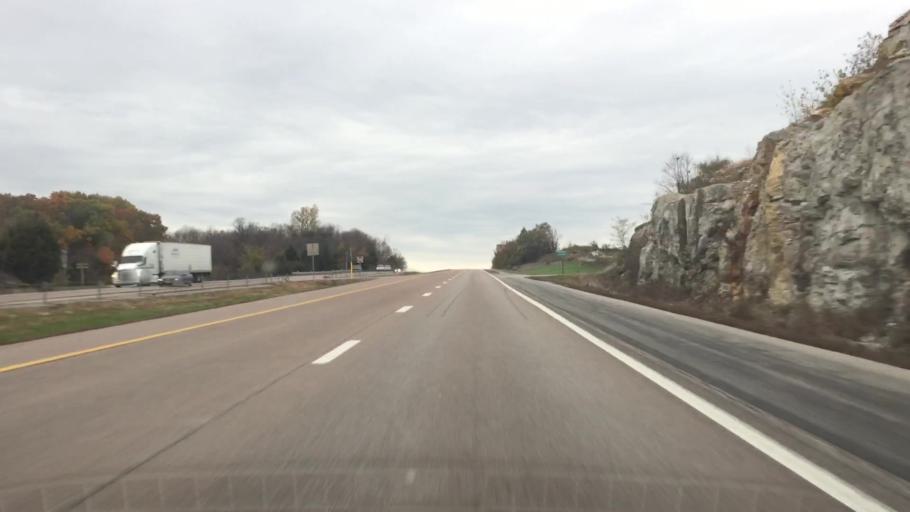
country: US
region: Missouri
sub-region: Boone County
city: Ashland
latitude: 38.6716
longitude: -92.2359
